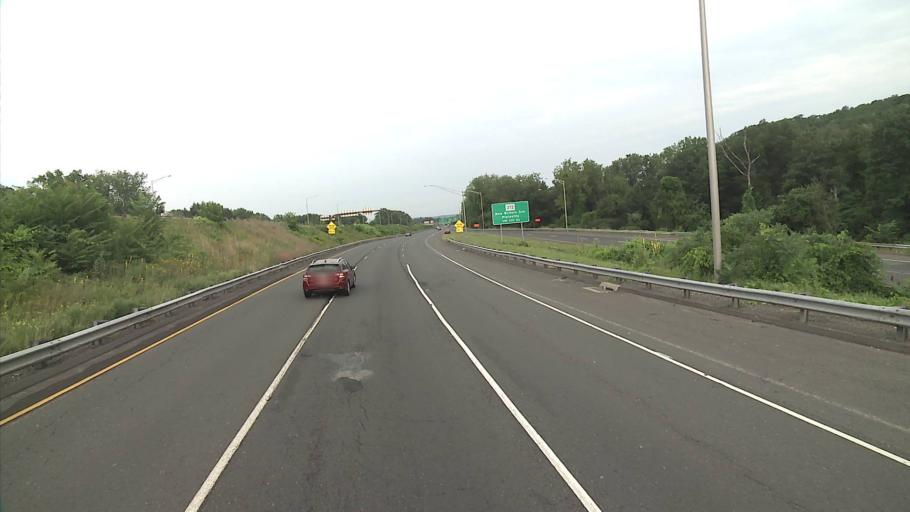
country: US
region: Connecticut
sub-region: Hartford County
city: Plainville
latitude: 41.6688
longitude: -72.8278
